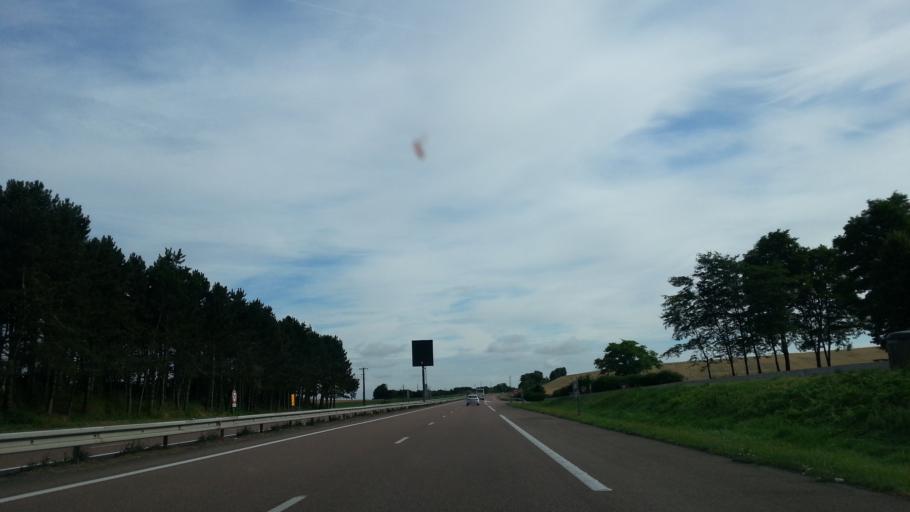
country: FR
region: Champagne-Ardenne
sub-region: Departement de la Marne
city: Chatillon-sur-Marne
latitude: 49.1883
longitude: 3.7532
